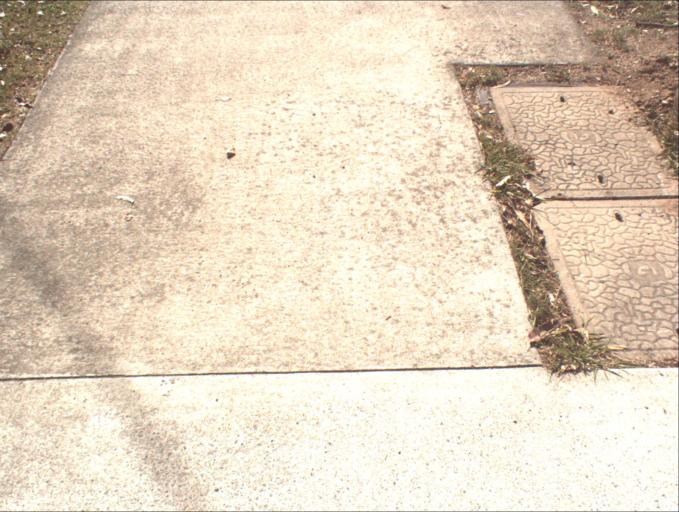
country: AU
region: Queensland
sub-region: Logan
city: Rochedale South
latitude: -27.5946
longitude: 153.1159
